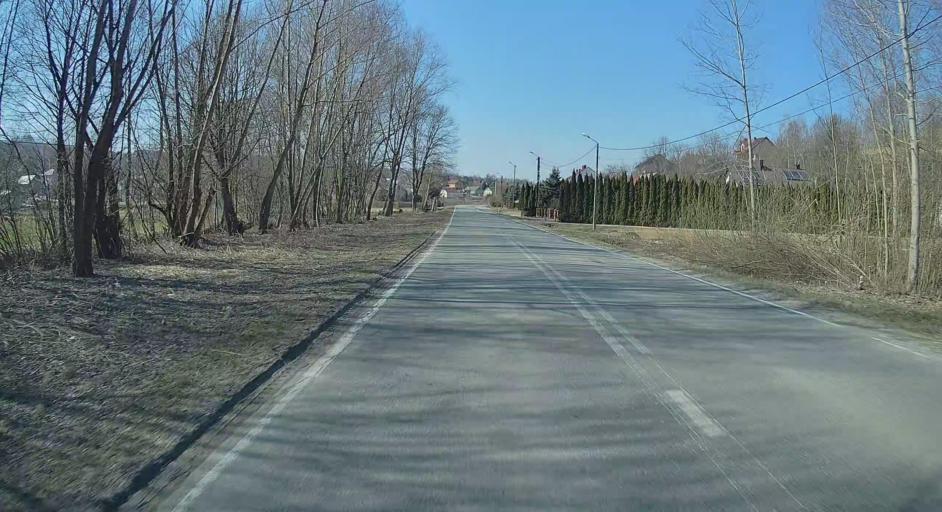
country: PL
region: Subcarpathian Voivodeship
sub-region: Powiat rzeszowski
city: Hyzne
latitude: 49.9149
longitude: 22.1882
